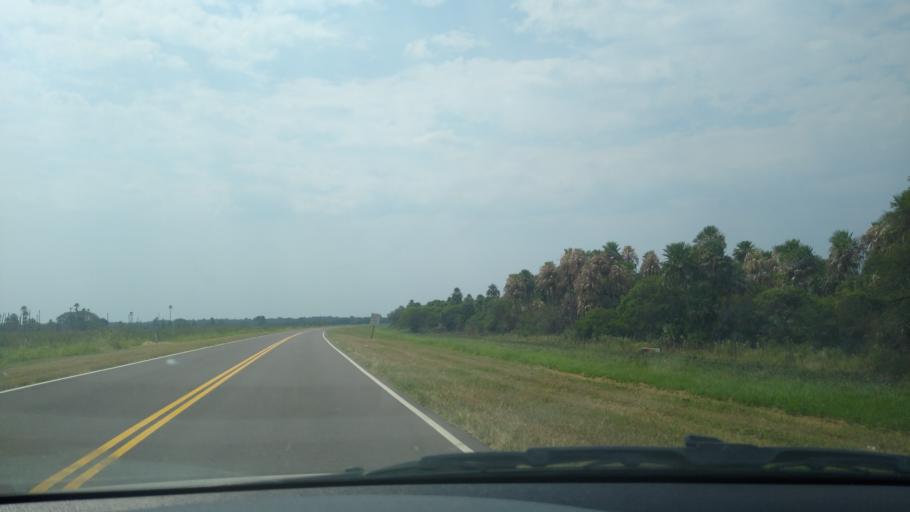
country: AR
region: Chaco
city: Margarita Belen
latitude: -27.0723
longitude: -58.9626
